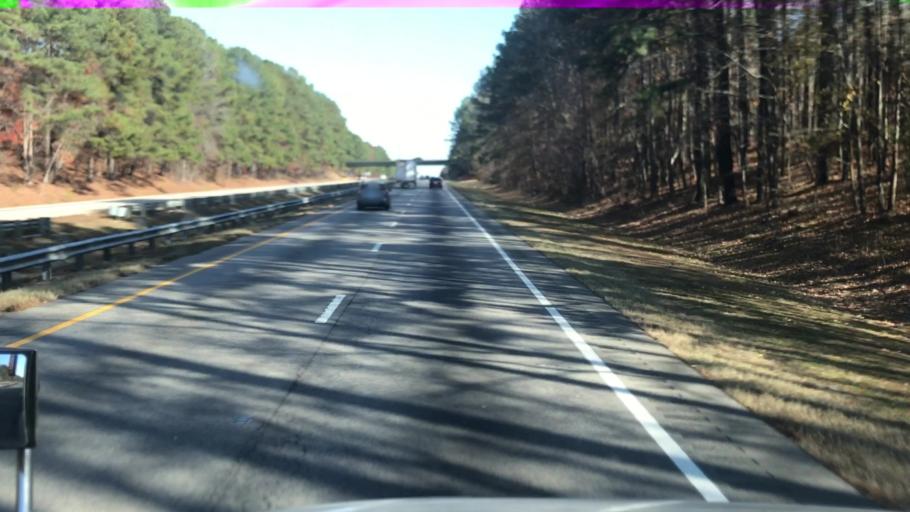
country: US
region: North Carolina
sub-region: Wake County
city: Wendell
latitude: 35.8152
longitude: -78.4027
